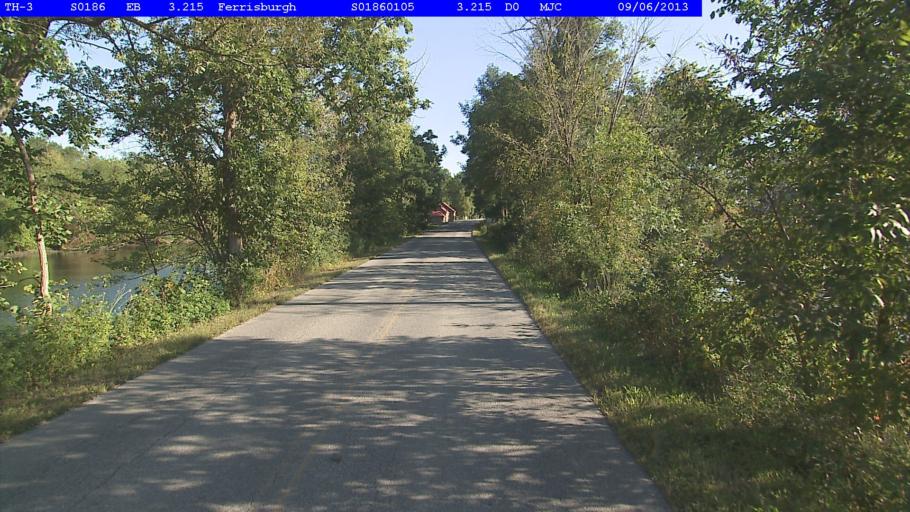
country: US
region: Vermont
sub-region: Addison County
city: Vergennes
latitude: 44.1802
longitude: -73.3087
